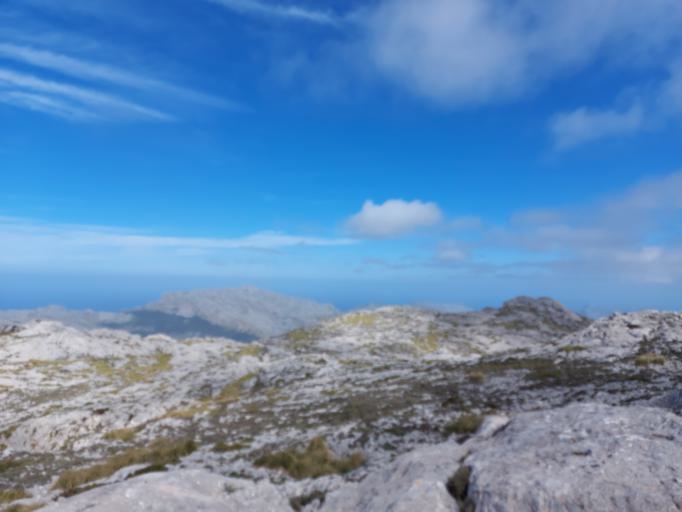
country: ES
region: Balearic Islands
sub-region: Illes Balears
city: Campanet
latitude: 39.8409
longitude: 2.9412
